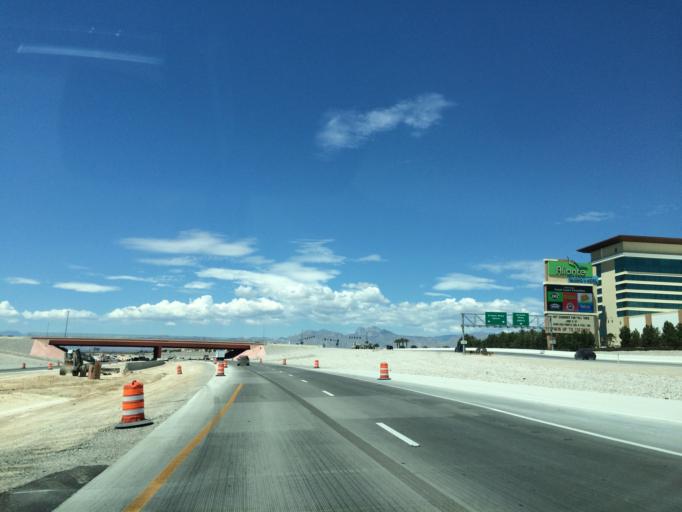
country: US
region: Nevada
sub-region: Clark County
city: North Las Vegas
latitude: 36.2918
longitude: -115.1776
